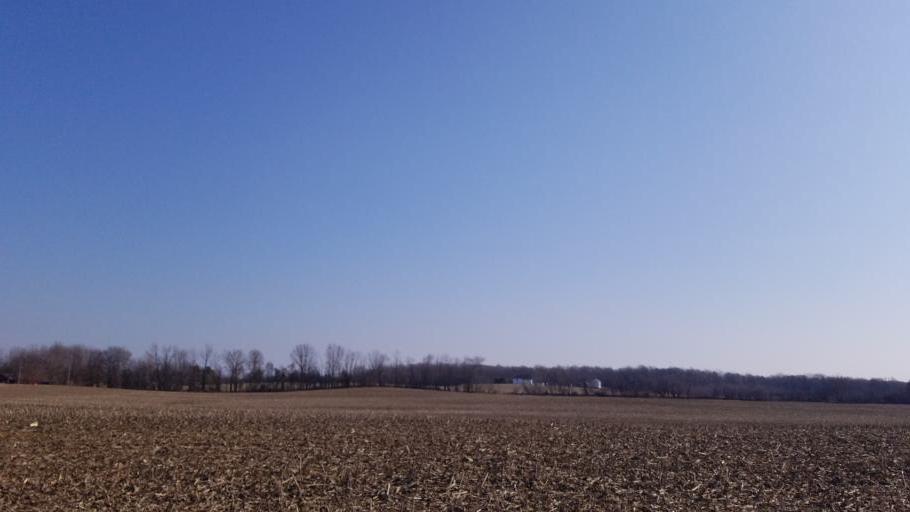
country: US
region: Ohio
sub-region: Richland County
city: Mansfield
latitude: 40.8280
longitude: -82.5424
